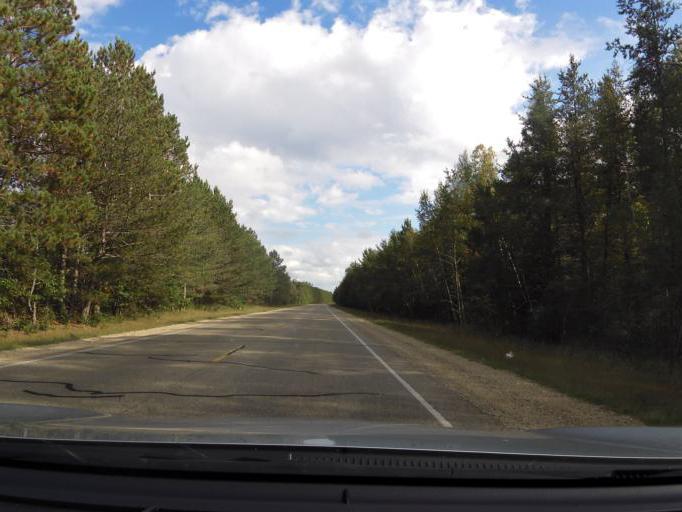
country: US
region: Michigan
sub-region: Roscommon County
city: Saint Helen
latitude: 44.4105
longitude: -84.4587
